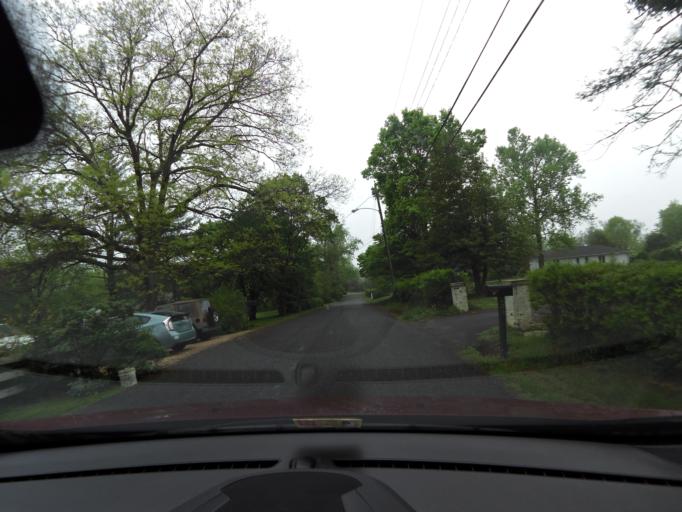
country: US
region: Virginia
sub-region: City of Lexington
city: Lexington
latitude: 37.7760
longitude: -79.4544
